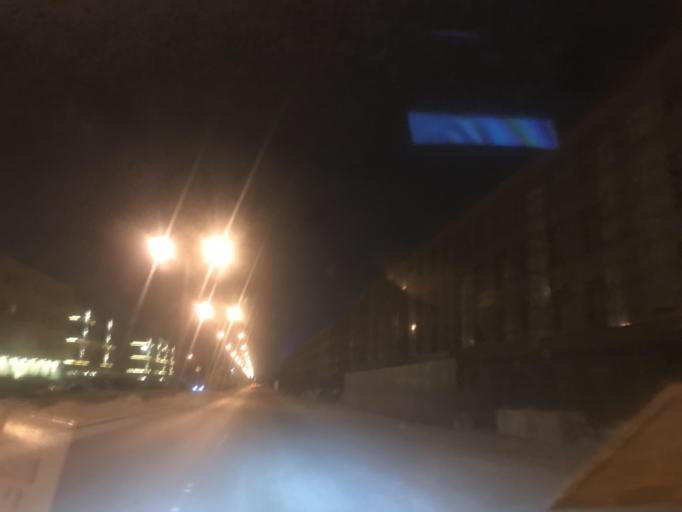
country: SA
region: Ar Riyad
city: Riyadh
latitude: 24.8057
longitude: 46.5909
